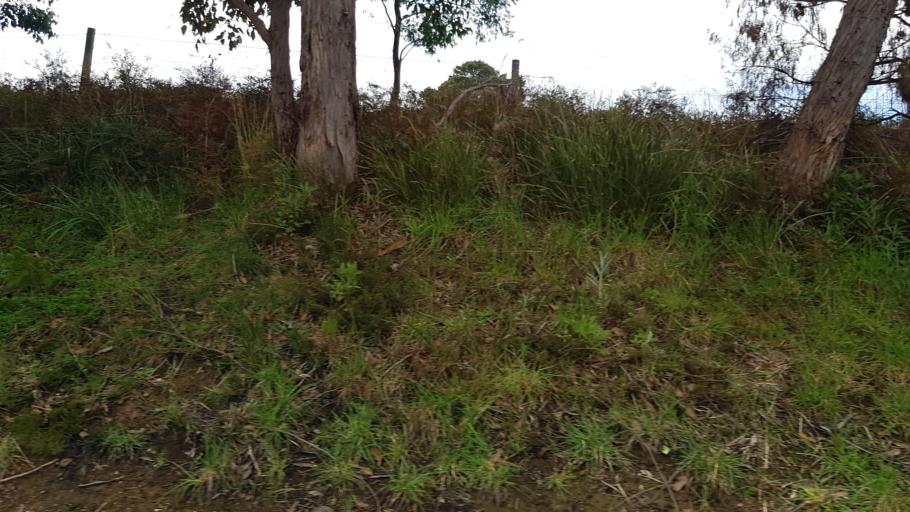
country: AU
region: Tasmania
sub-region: Huon Valley
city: Huonville
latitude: -42.9961
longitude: 147.0656
